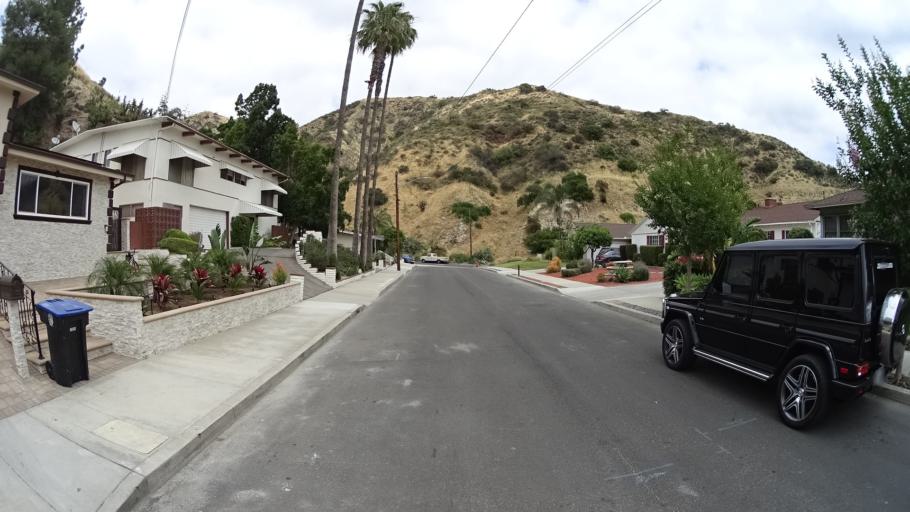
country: US
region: California
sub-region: Los Angeles County
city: Burbank
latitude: 34.2067
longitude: -118.3187
